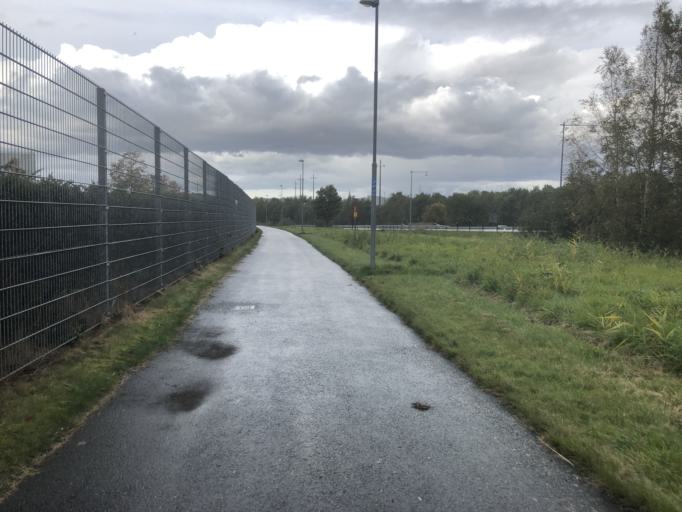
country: SE
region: Vaestra Goetaland
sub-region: Molndal
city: Moelndal
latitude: 57.6450
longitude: 12.0231
